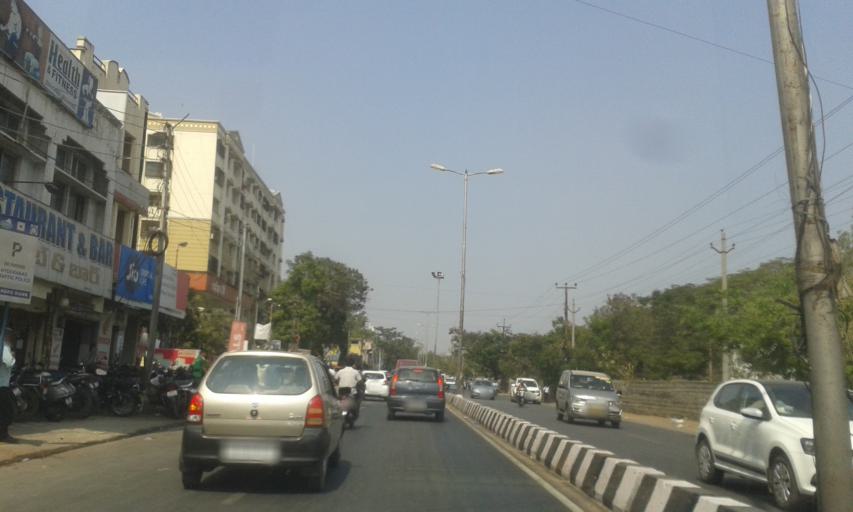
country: IN
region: Telangana
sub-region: Rangareddi
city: Secunderabad
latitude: 17.4986
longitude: 78.5135
